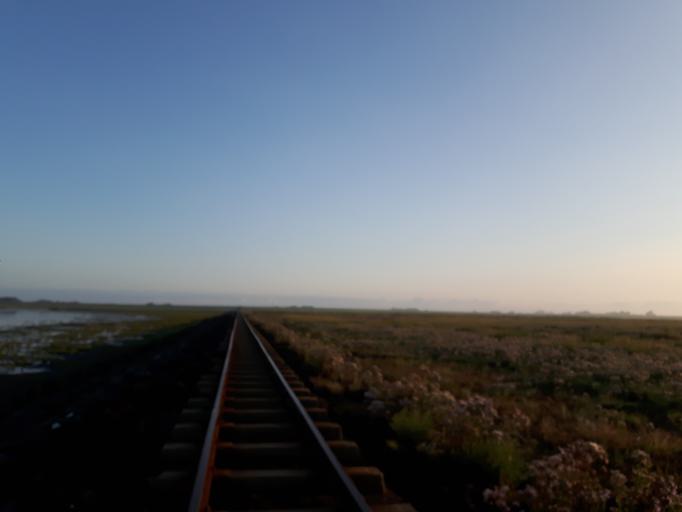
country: DE
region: Schleswig-Holstein
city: Dagebull
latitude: 54.7166
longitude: 8.7116
